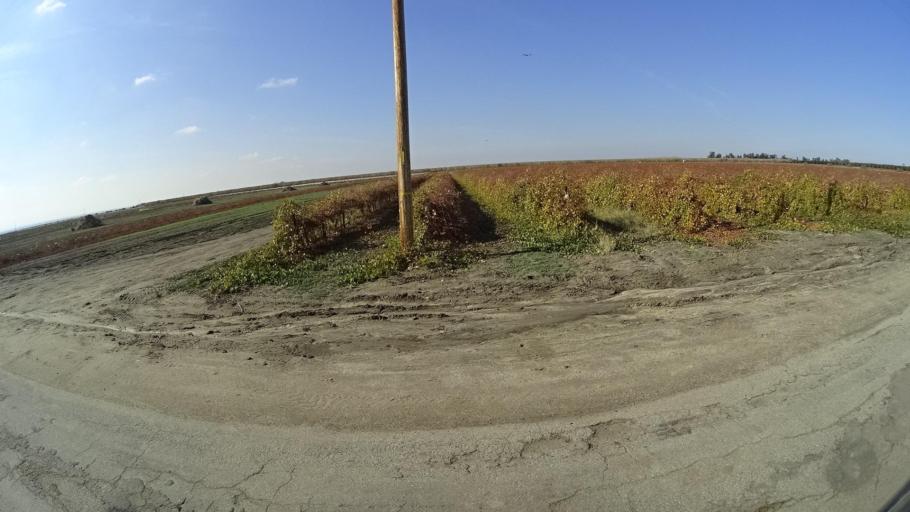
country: US
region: California
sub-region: Kern County
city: Arvin
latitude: 35.2854
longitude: -118.7709
